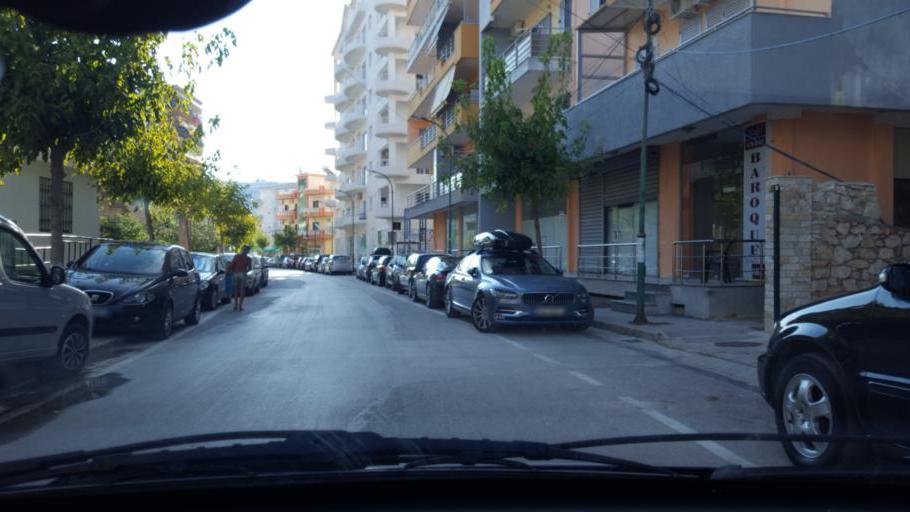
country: AL
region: Vlore
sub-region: Rrethi i Sarandes
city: Sarande
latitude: 39.8689
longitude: 20.0001
